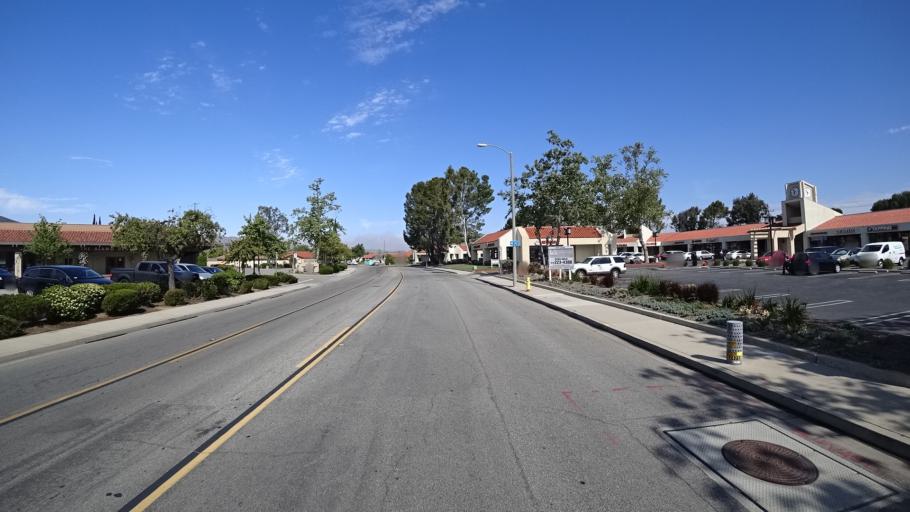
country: US
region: California
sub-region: Ventura County
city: Casa Conejo
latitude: 34.1824
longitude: -118.9281
